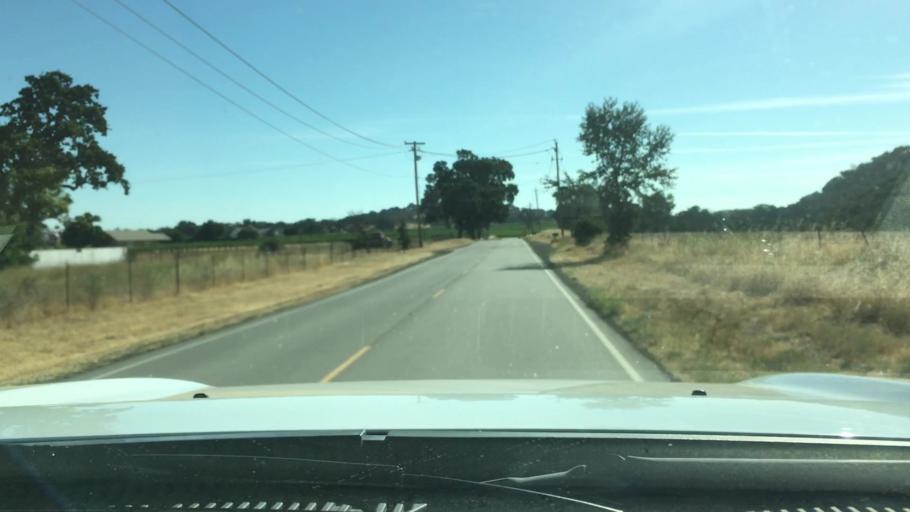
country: US
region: California
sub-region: San Luis Obispo County
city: Templeton
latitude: 35.5600
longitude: -120.6726
